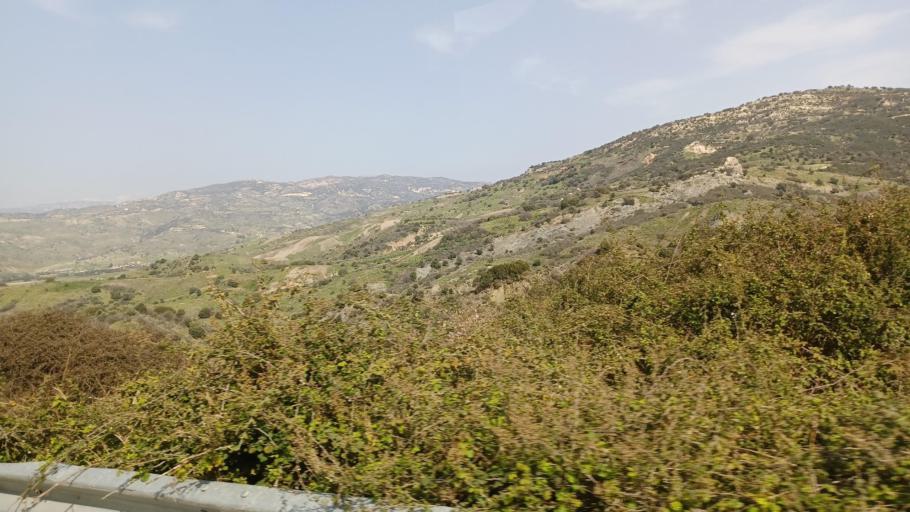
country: CY
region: Limassol
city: Pissouri
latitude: 34.7538
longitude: 32.6522
